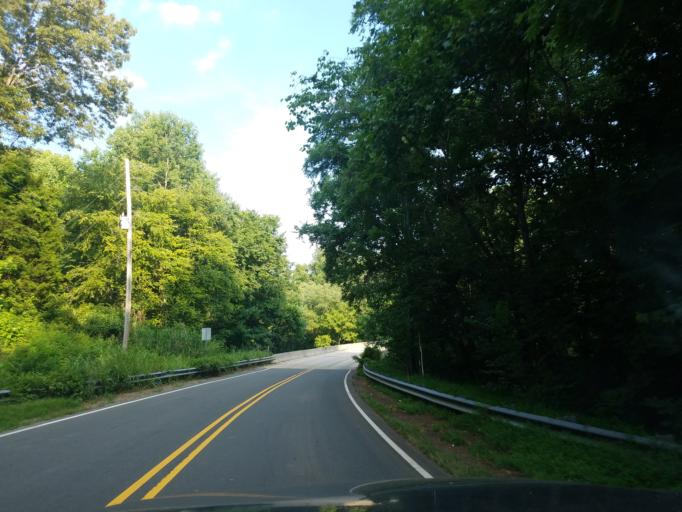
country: US
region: North Carolina
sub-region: Granville County
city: Butner
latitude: 36.2281
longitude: -78.8896
